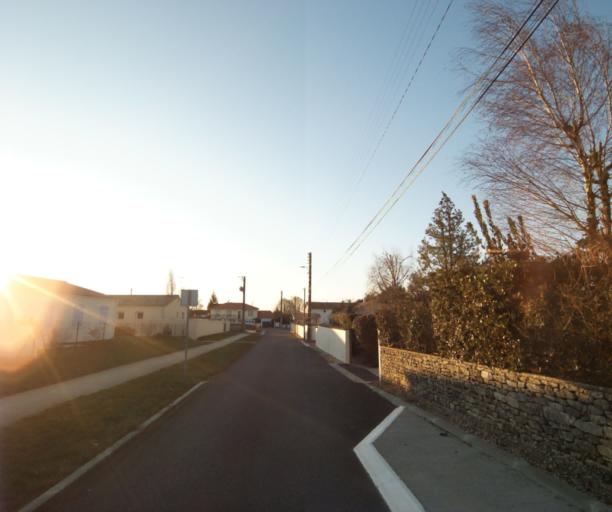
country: FR
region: Poitou-Charentes
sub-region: Departement des Deux-Sevres
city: Niort
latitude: 46.3563
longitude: -0.4505
